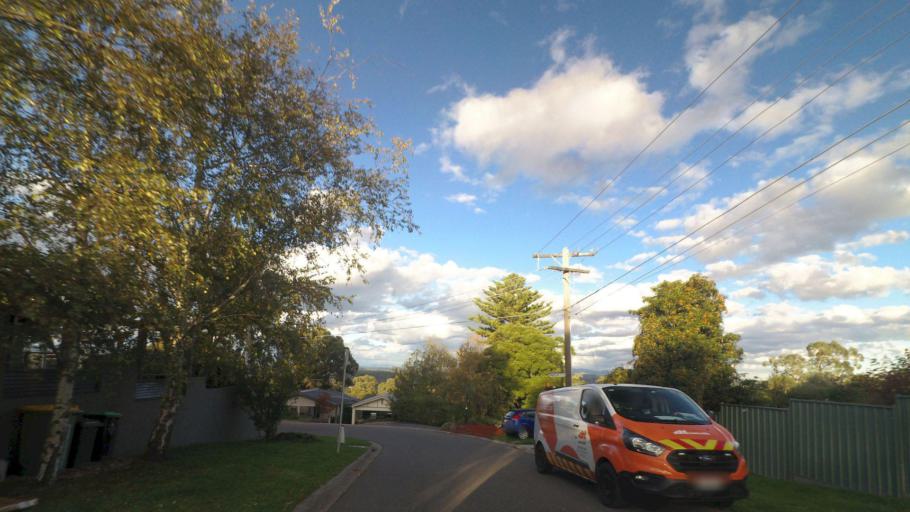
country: AU
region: Victoria
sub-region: Banyule
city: Lower Plenty
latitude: -37.7301
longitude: 145.1243
